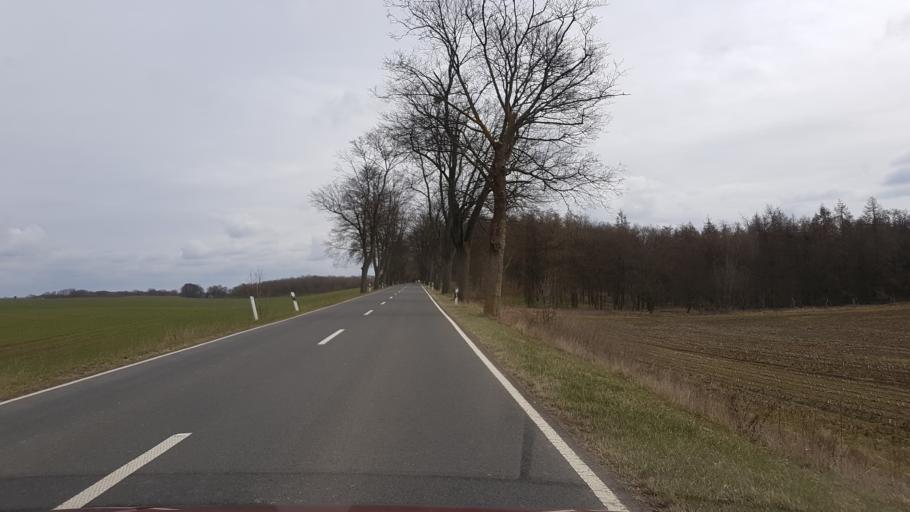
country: DE
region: Brandenburg
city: Mescherin
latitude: 53.2656
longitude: 14.4161
